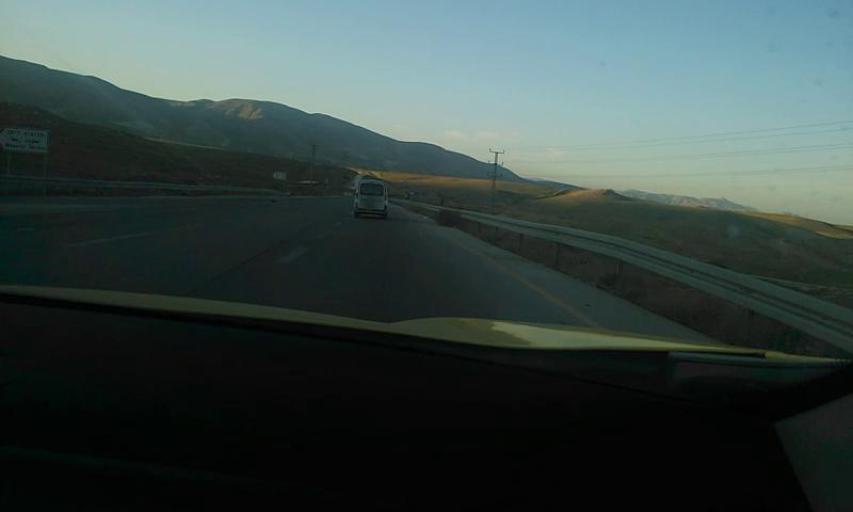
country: PS
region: West Bank
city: An Nuway`imah
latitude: 31.9158
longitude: 35.4205
